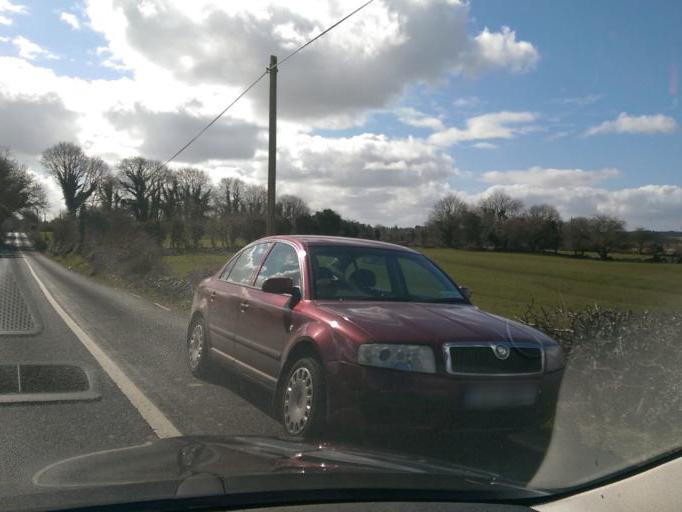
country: IE
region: Connaught
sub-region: County Galway
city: Athenry
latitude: 53.3944
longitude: -8.6581
